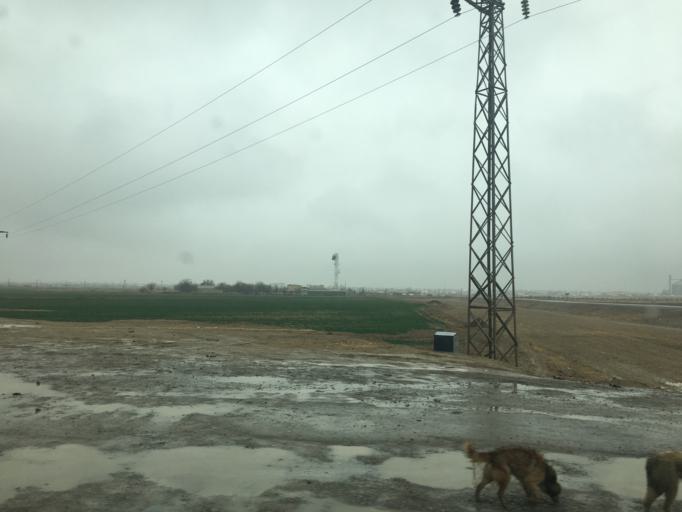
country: TM
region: Mary
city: Bayramaly
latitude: 37.4116
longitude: 62.1645
